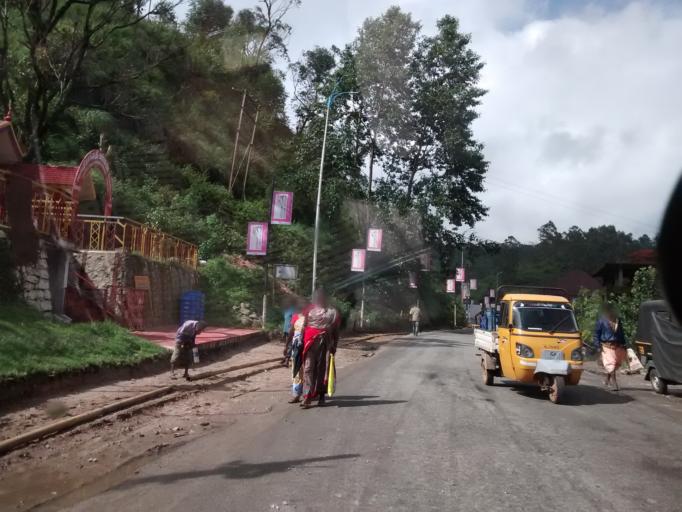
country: IN
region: Kerala
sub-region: Idukki
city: Munnar
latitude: 10.0739
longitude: 77.0622
